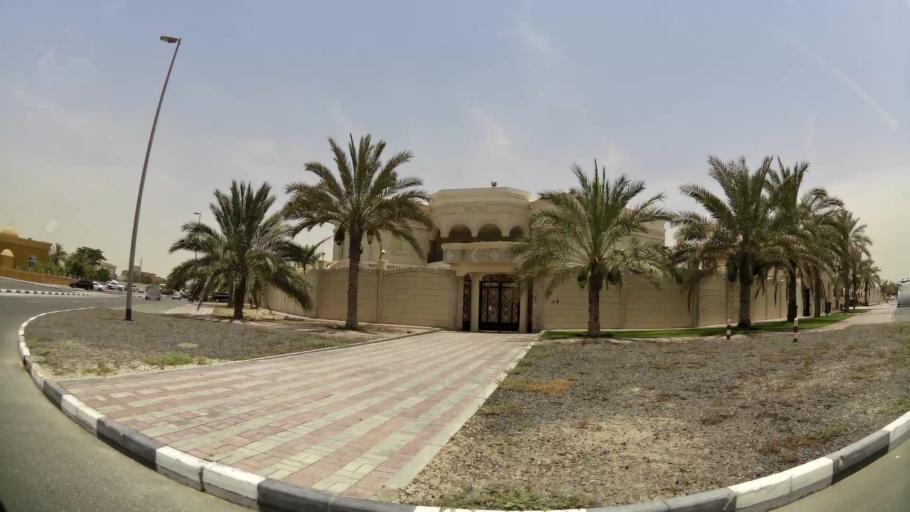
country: AE
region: Ash Shariqah
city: Sharjah
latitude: 25.2100
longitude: 55.3818
